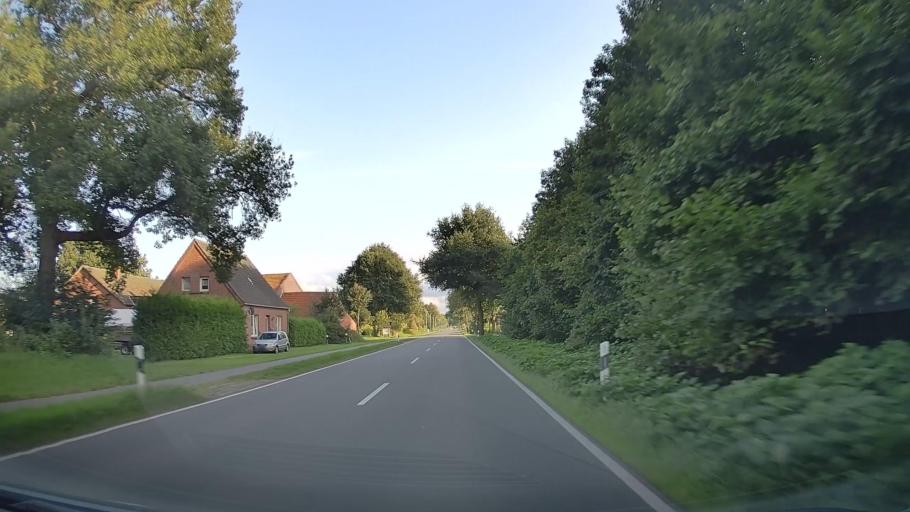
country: DE
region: Lower Saxony
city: Hilkenbrook
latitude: 53.0544
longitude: 7.7285
